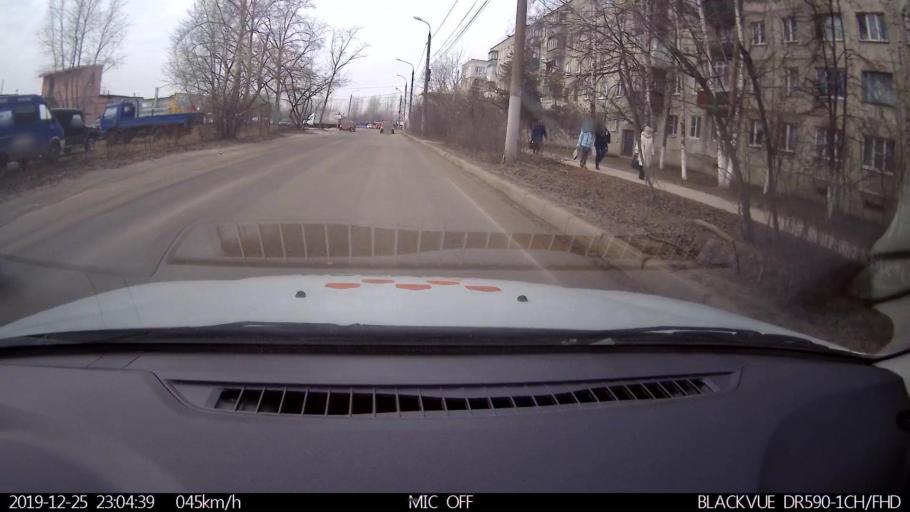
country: RU
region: Nizjnij Novgorod
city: Gorbatovka
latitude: 56.3584
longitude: 43.8076
